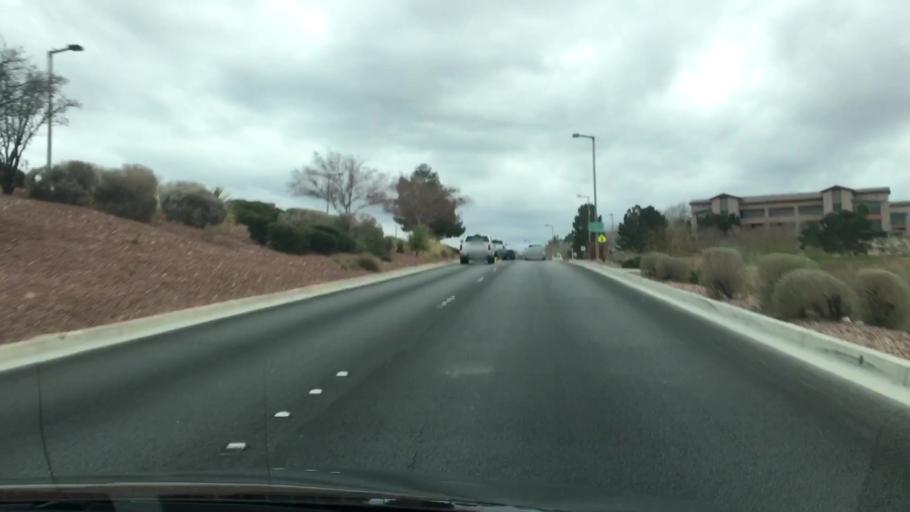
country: US
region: Nevada
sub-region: Clark County
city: Whitney
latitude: 35.9590
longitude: -115.0950
